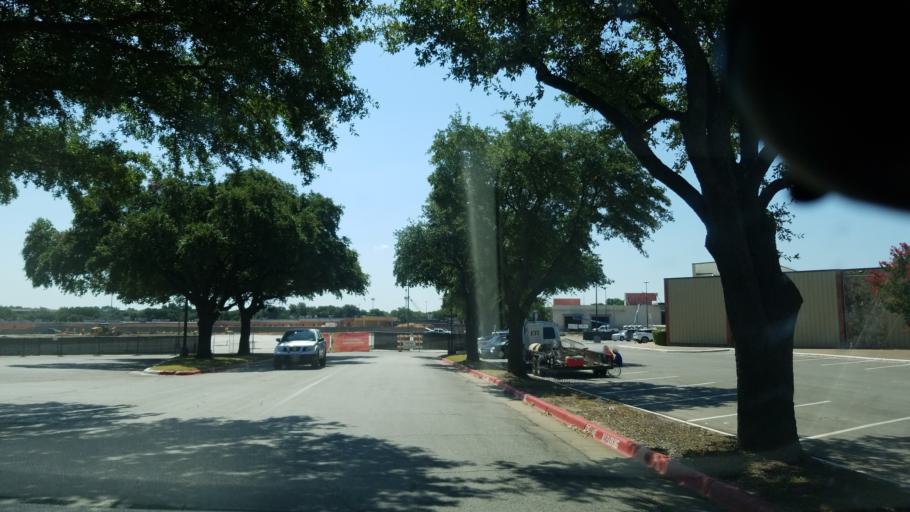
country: US
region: Texas
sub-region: Dallas County
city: Cockrell Hill
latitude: 32.7233
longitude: -96.8352
